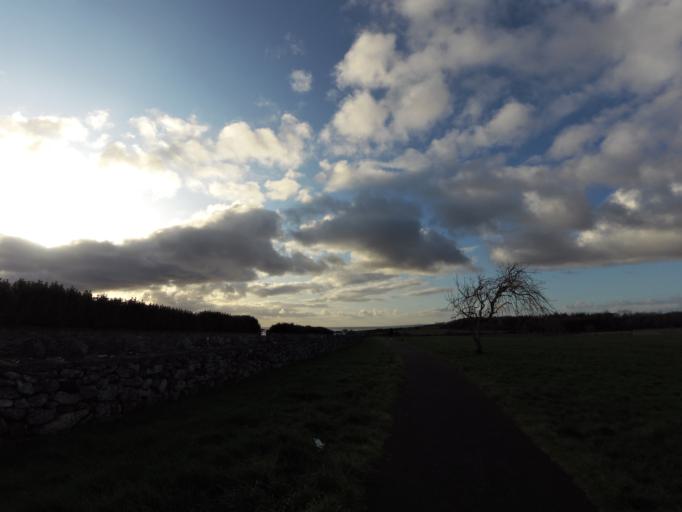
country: IE
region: Connaught
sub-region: County Galway
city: Oranmore
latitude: 53.2458
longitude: -8.9577
